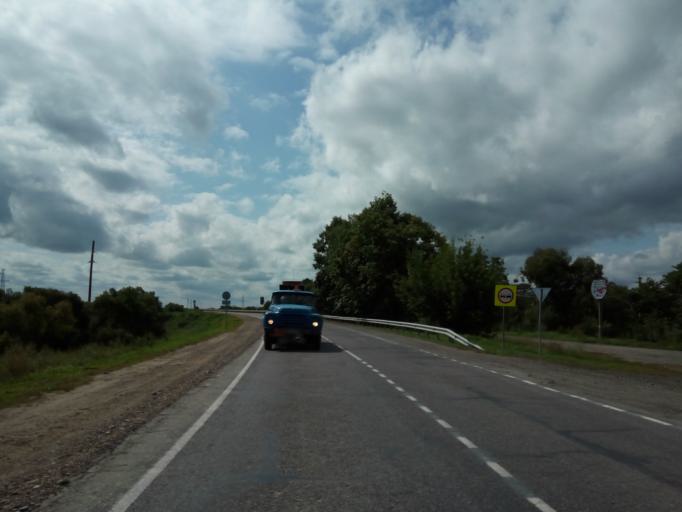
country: RU
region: Primorskiy
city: Dal'nerechensk
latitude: 45.9666
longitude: 133.7832
